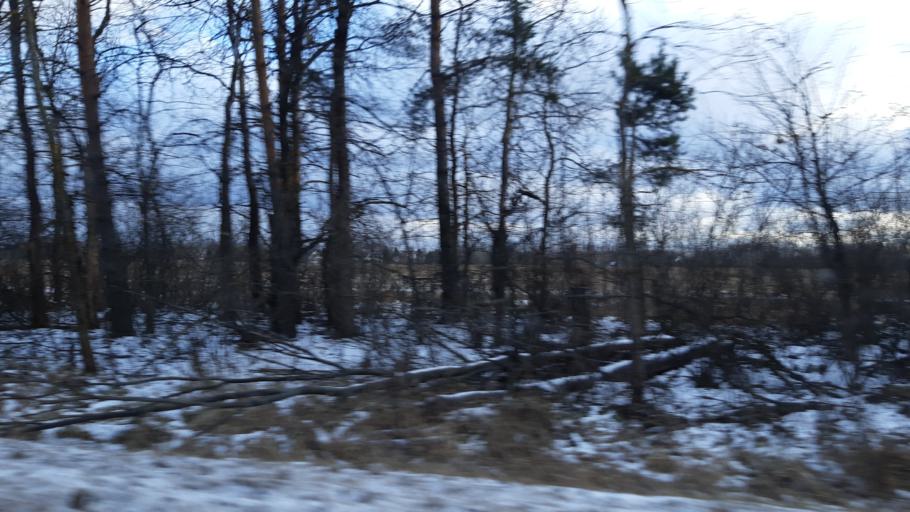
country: RU
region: Moskovskaya
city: Noginsk-9
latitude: 56.0065
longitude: 38.5564
